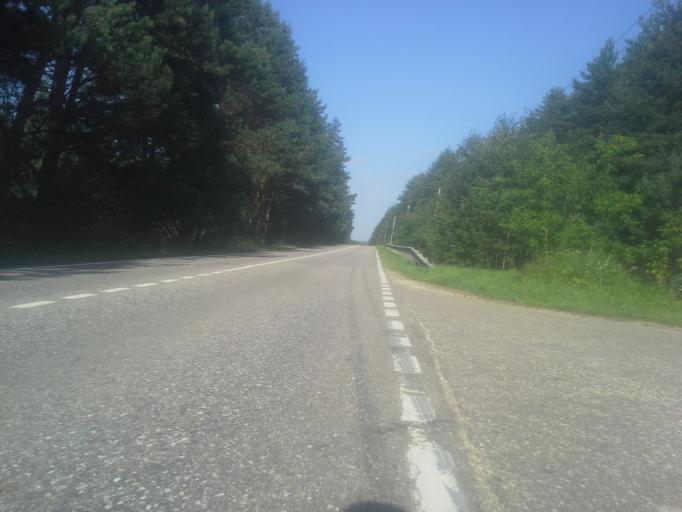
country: RU
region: Moskovskaya
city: Karinskoye
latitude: 55.7020
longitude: 36.7476
